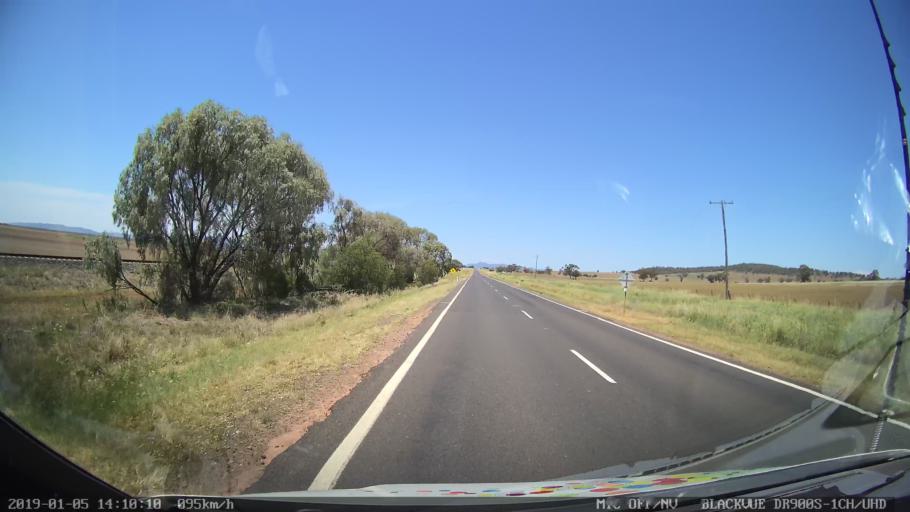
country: AU
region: New South Wales
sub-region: Gunnedah
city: Gunnedah
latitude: -31.2466
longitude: 150.4380
